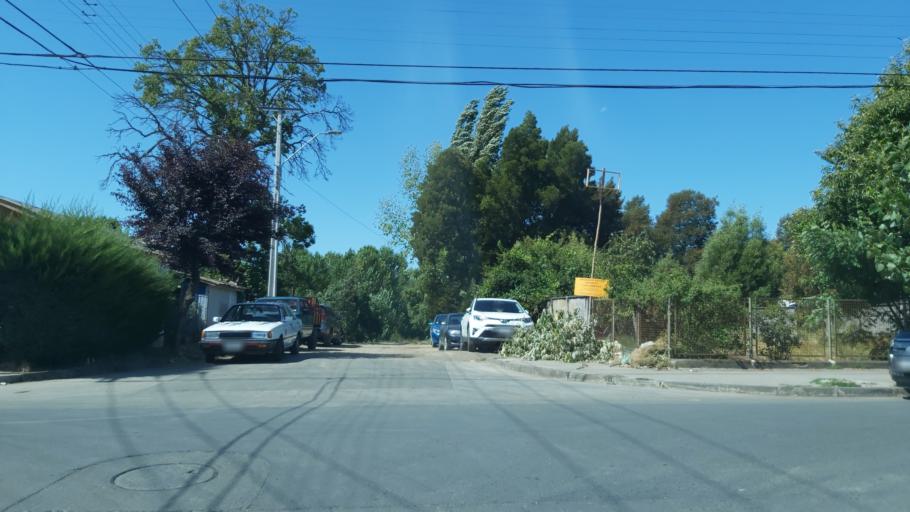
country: CL
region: Biobio
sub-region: Provincia de Concepcion
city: Lota
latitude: -37.1733
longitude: -72.9369
